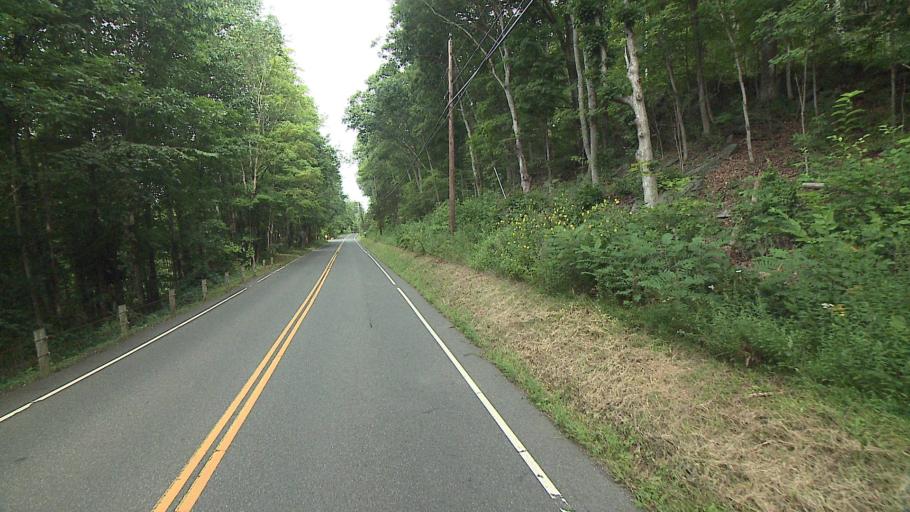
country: US
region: Connecticut
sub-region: Litchfield County
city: Woodbury
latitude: 41.5766
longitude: -73.2382
